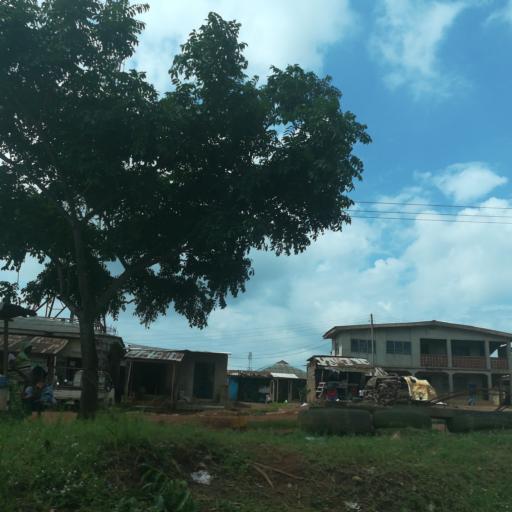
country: NG
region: Lagos
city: Ejirin
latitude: 6.6492
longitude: 3.7118
